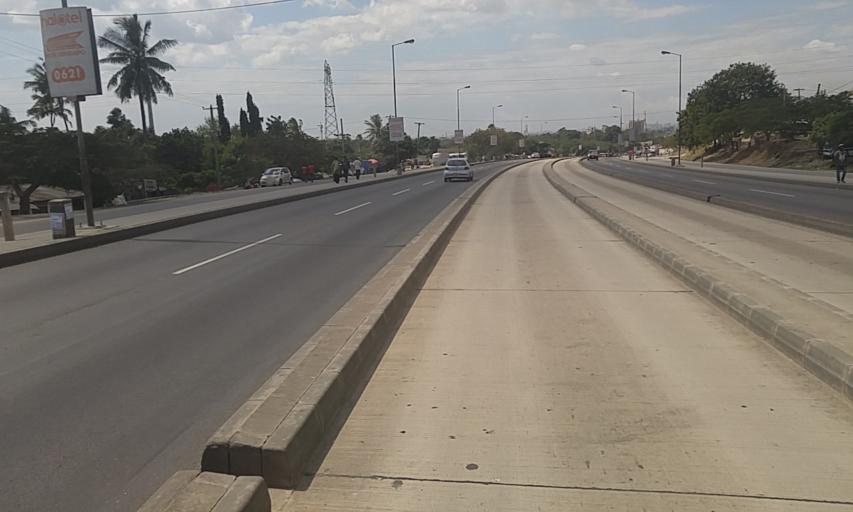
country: TZ
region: Dar es Salaam
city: Magomeni
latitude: -6.7905
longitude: 39.1999
